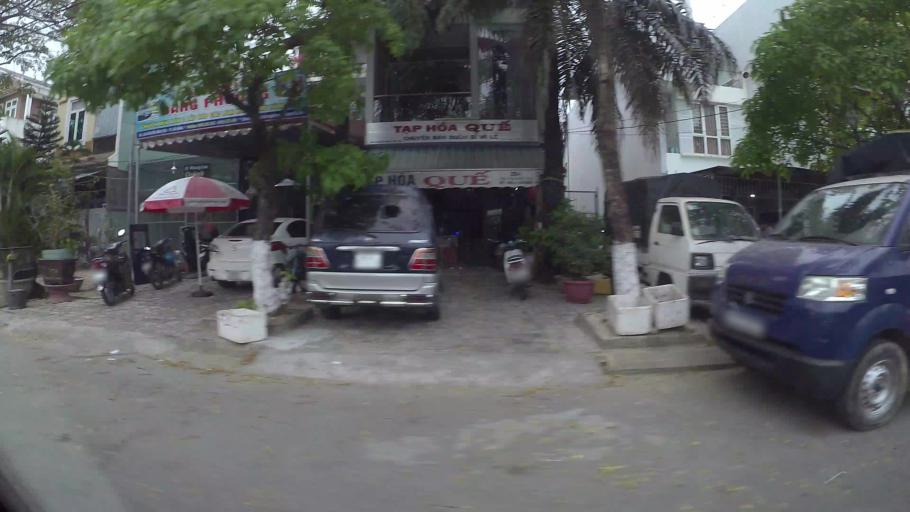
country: VN
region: Da Nang
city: Thanh Khe
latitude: 16.0561
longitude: 108.1845
